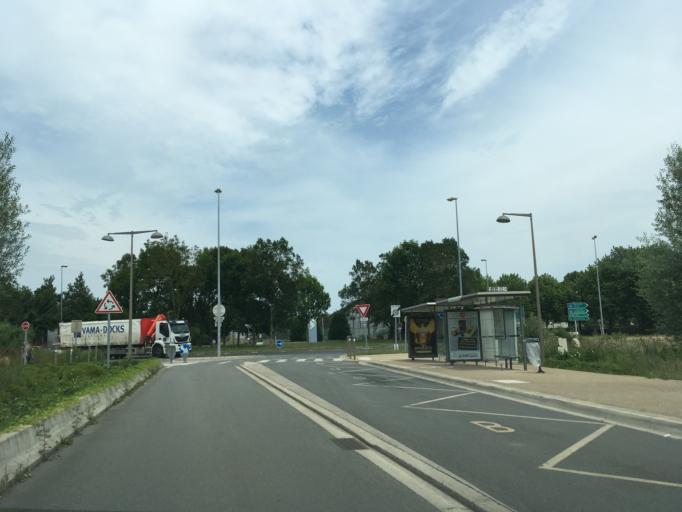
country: FR
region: Poitou-Charentes
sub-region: Departement des Deux-Sevres
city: Niort
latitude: 46.3269
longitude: -0.4901
